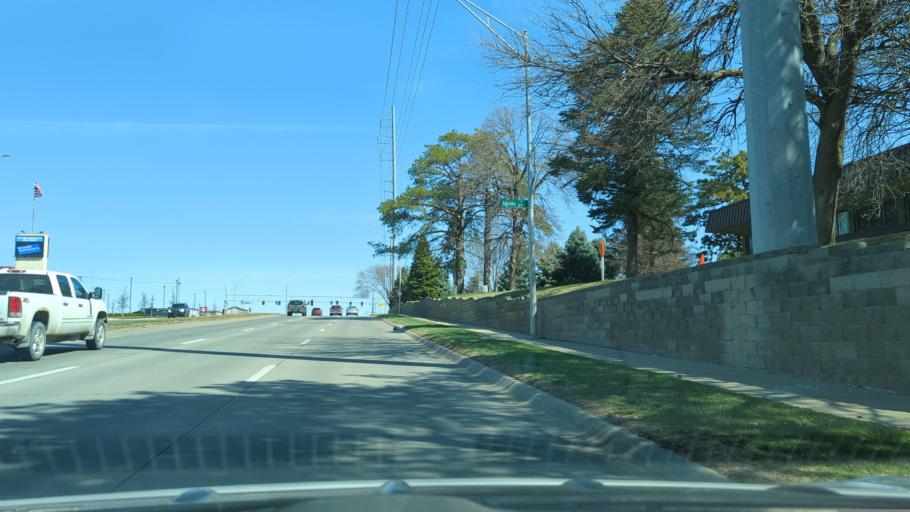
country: US
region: Nebraska
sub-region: Douglas County
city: Ralston
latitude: 41.2413
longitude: -96.0239
